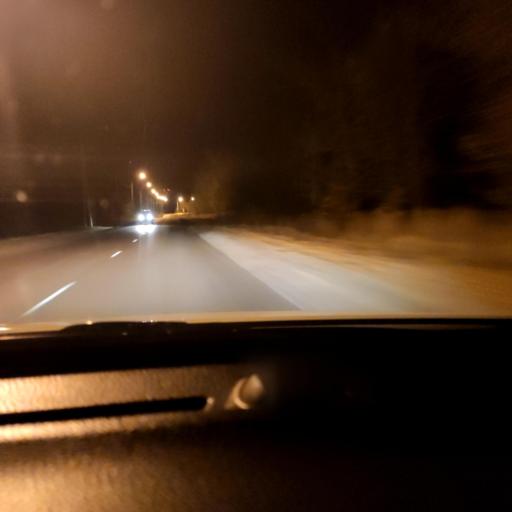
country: RU
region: Voronezj
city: Somovo
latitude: 51.7282
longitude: 39.3188
